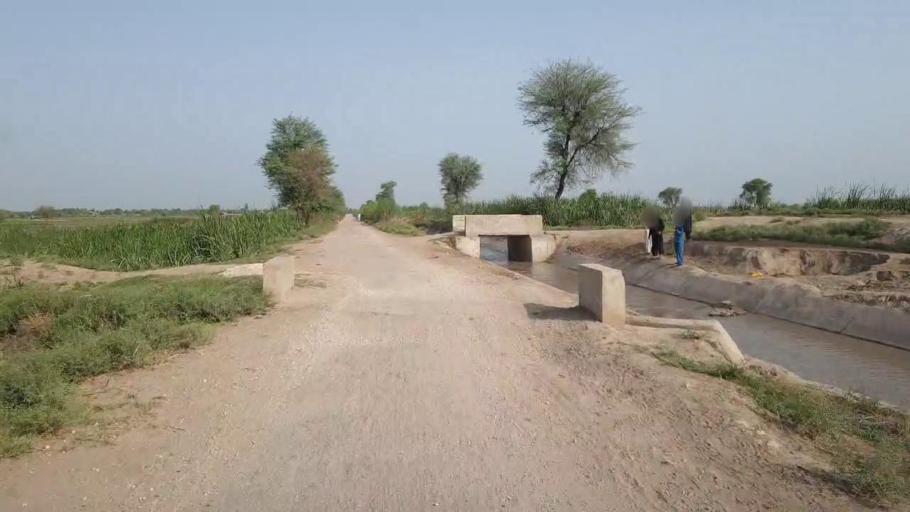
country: PK
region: Sindh
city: Daur
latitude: 26.3364
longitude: 68.1856
